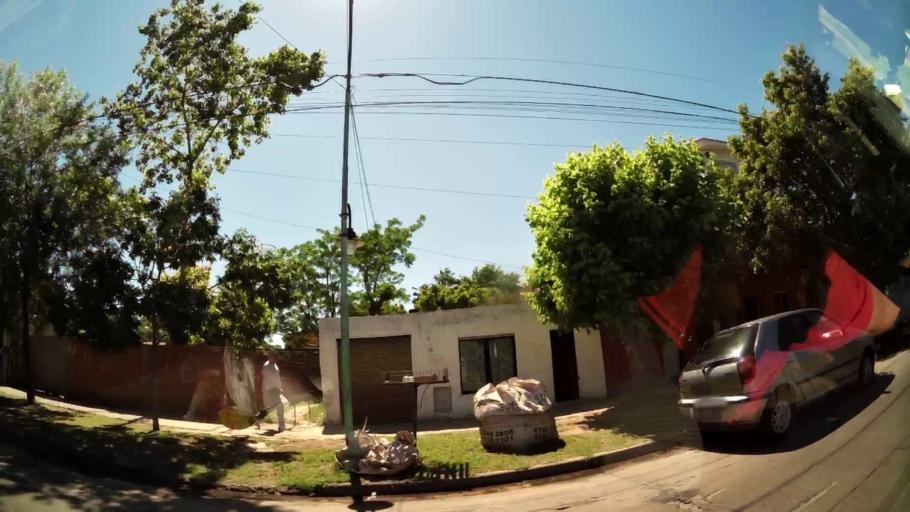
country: AR
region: Buenos Aires
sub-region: Partido de Tigre
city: Tigre
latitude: -34.4953
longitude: -58.6162
